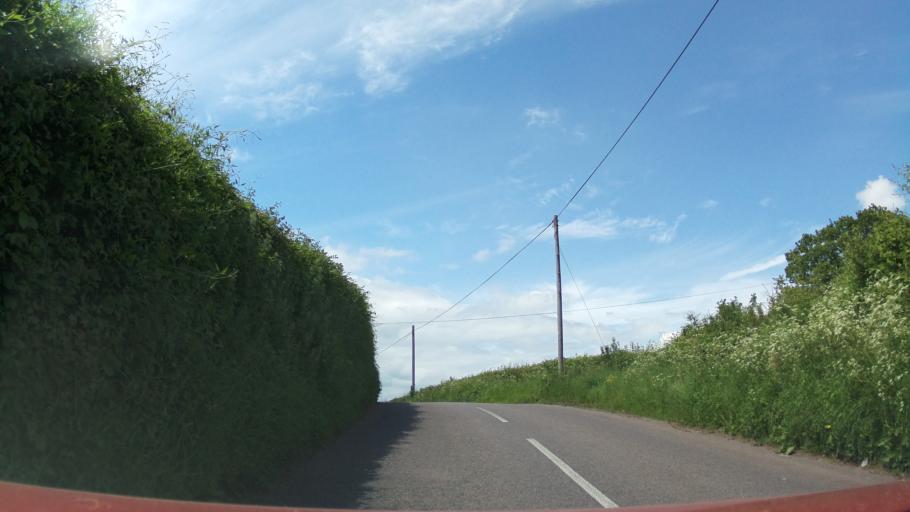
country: GB
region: England
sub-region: Herefordshire
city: Llanrothal
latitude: 51.8346
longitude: -2.7593
